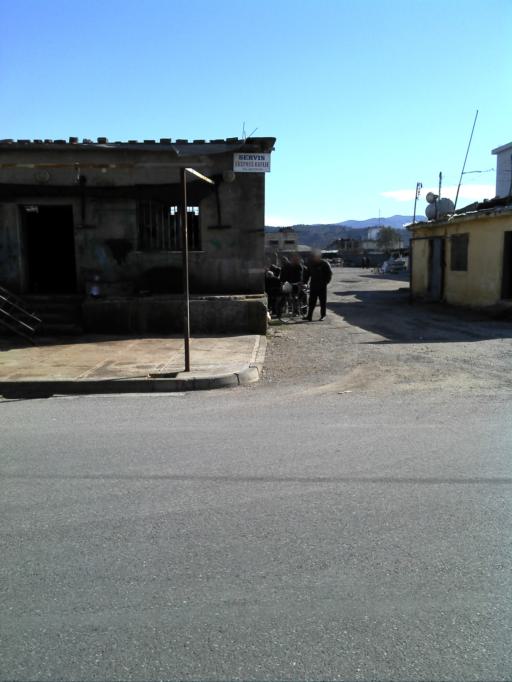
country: AL
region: Shkoder
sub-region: Rrethi i Shkodres
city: Shkoder
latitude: 42.0803
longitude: 19.5286
